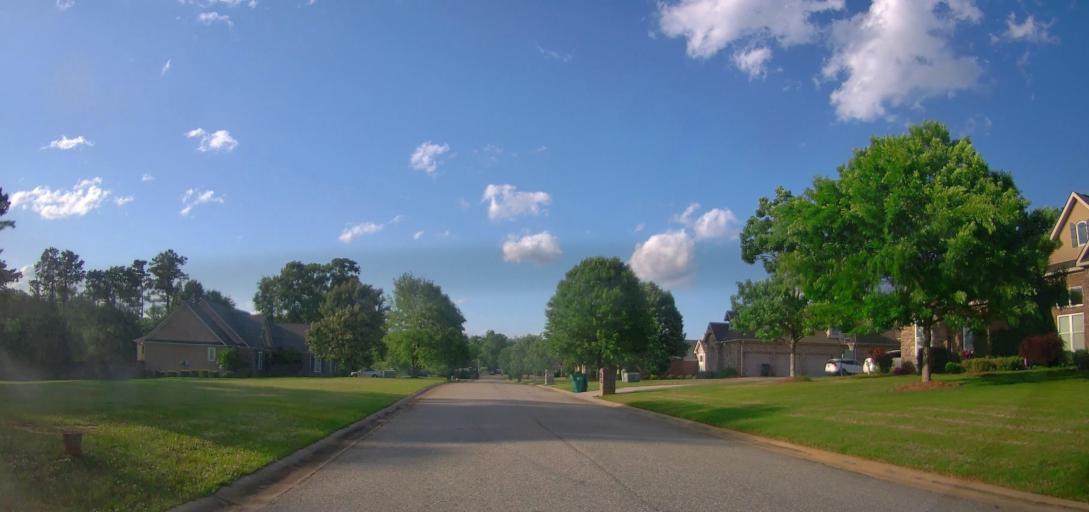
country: US
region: Georgia
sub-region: Peach County
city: Byron
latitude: 32.6449
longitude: -83.7935
